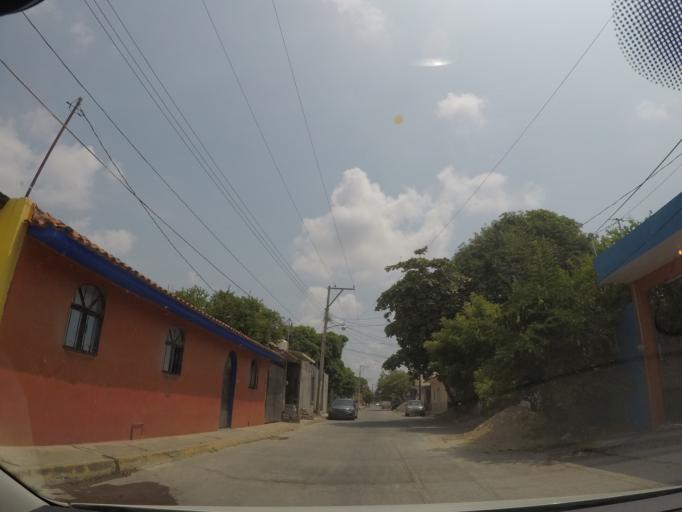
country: MX
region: Oaxaca
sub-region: El Espinal
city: El Espinal
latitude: 16.4818
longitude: -95.0407
